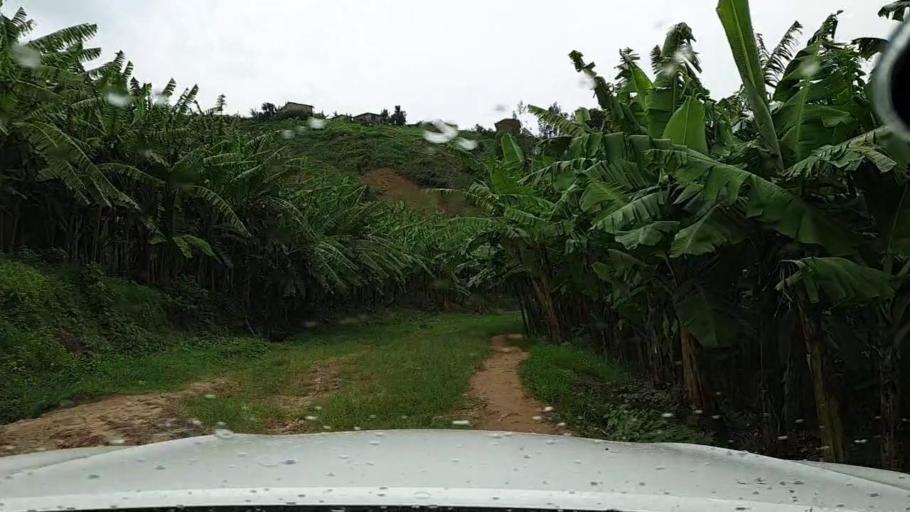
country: RW
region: Kigali
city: Kigali
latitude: -1.9001
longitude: 29.9533
